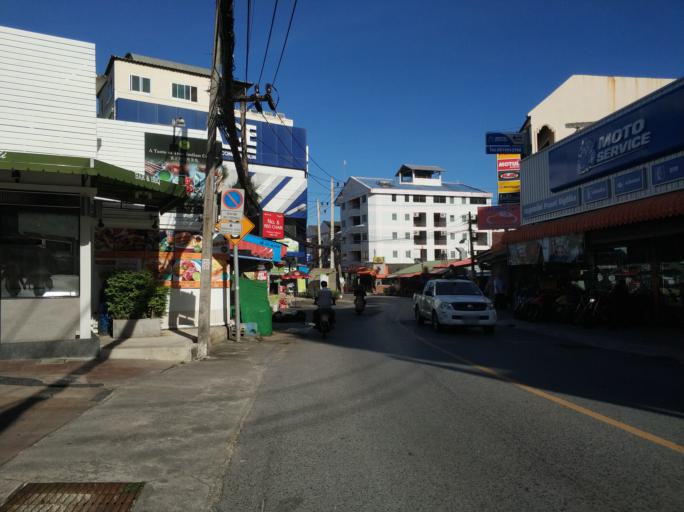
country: TH
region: Phuket
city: Patong
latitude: 7.8956
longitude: 98.3038
